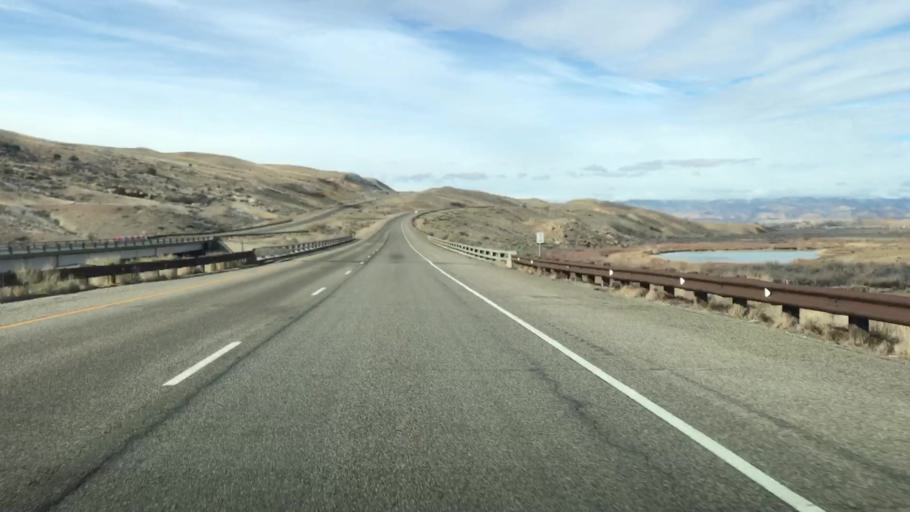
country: US
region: Colorado
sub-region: Mesa County
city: Loma
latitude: 39.2241
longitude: -108.8911
